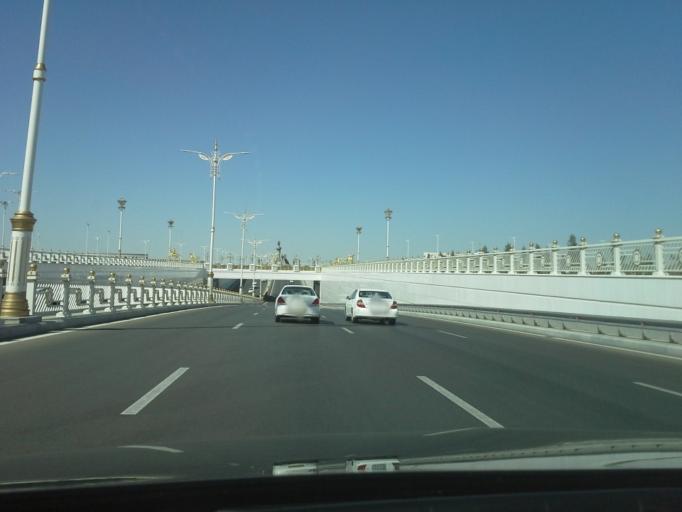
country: TM
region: Ahal
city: Ashgabat
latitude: 37.9690
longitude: 58.3864
